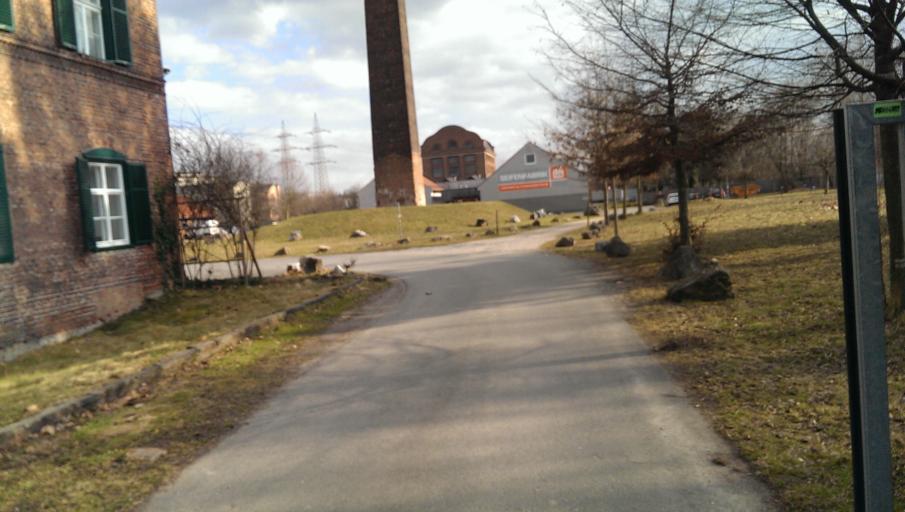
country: AT
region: Styria
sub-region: Graz Stadt
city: Graz
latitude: 47.0485
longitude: 15.4414
